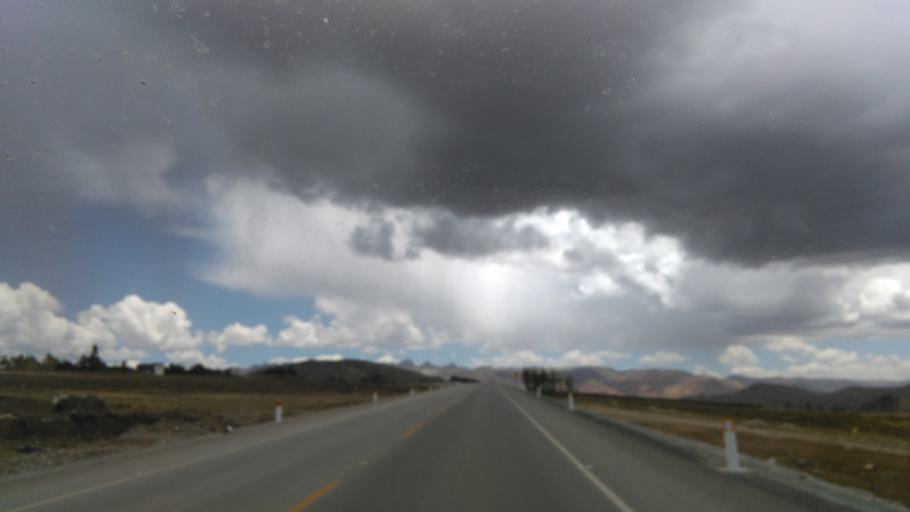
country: PE
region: Apurimac
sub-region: Provincia de Andahuaylas
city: San Jeronimo
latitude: -13.7235
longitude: -73.3513
